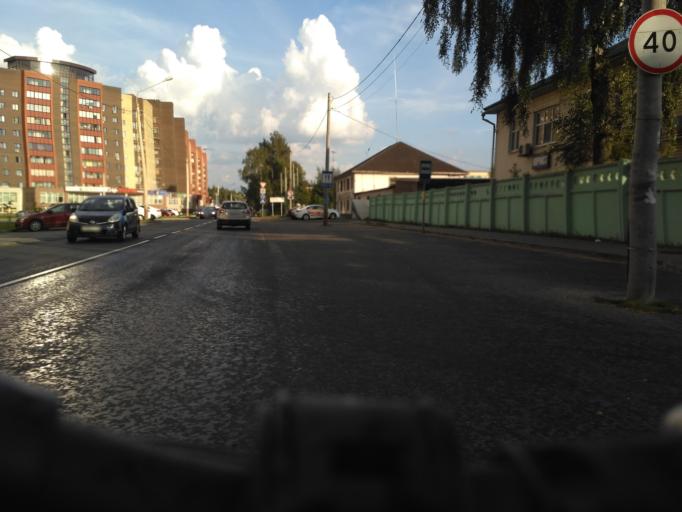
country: RU
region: Moskovskaya
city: Dubna
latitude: 56.7293
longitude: 37.1394
